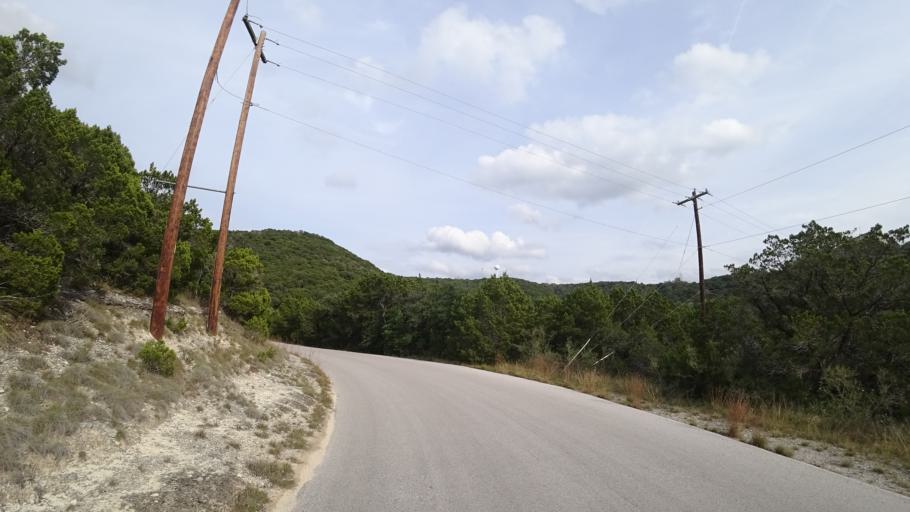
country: US
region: Texas
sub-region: Travis County
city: Hudson Bend
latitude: 30.3966
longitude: -97.8777
